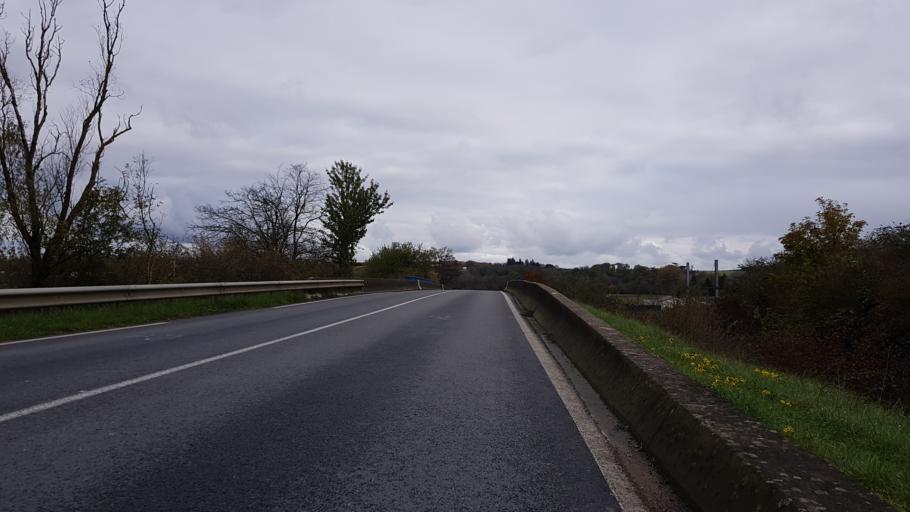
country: FR
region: Poitou-Charentes
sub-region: Departement de la Vienne
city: Chasseneuil-du-Poitou
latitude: 46.6635
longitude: 0.3770
